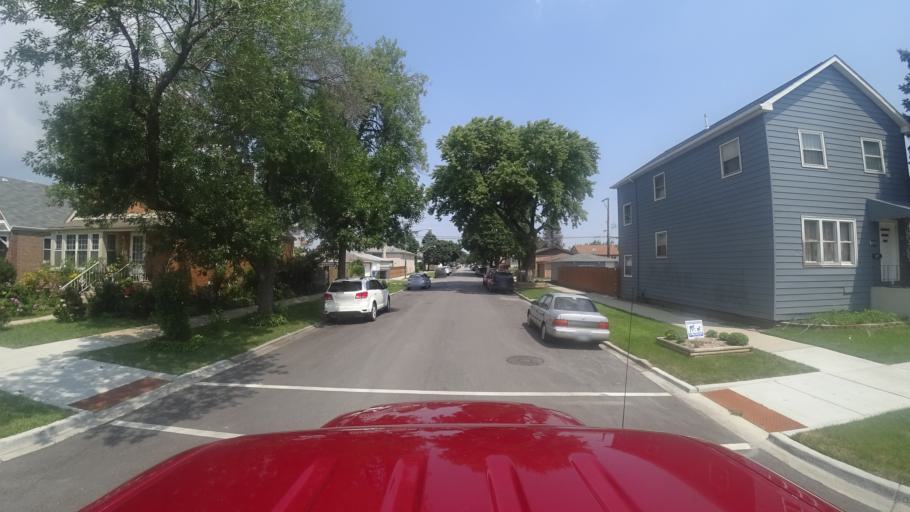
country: US
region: Illinois
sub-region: Cook County
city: Hometown
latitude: 41.7906
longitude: -87.7182
